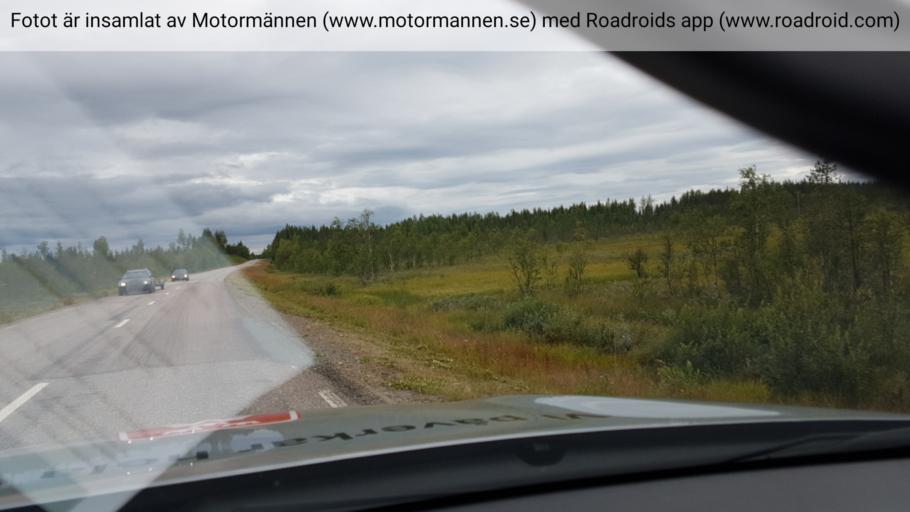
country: SE
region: Norrbotten
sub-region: Overkalix Kommun
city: OEverkalix
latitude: 66.8062
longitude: 22.9780
